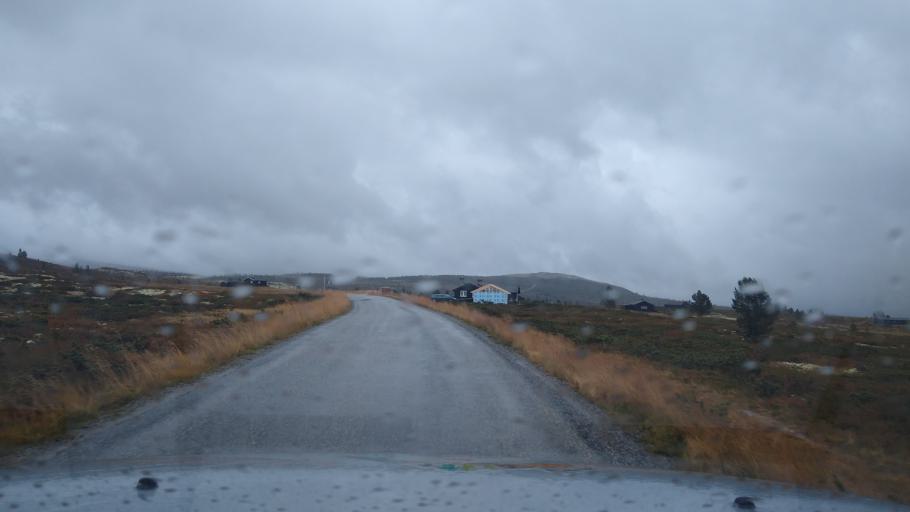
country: NO
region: Oppland
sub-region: Ringebu
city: Ringebu
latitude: 61.6710
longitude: 10.1110
